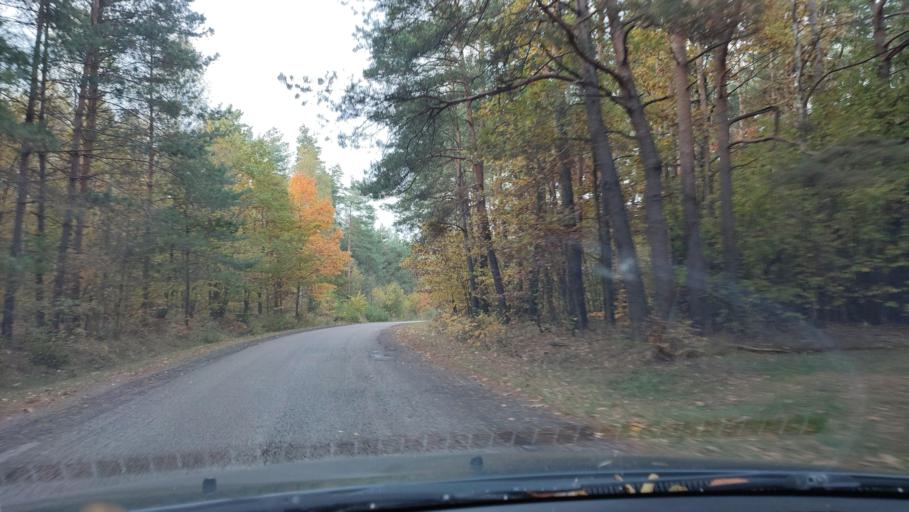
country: PL
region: Masovian Voivodeship
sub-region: Powiat mlawski
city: Mlawa
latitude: 53.1443
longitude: 20.3690
